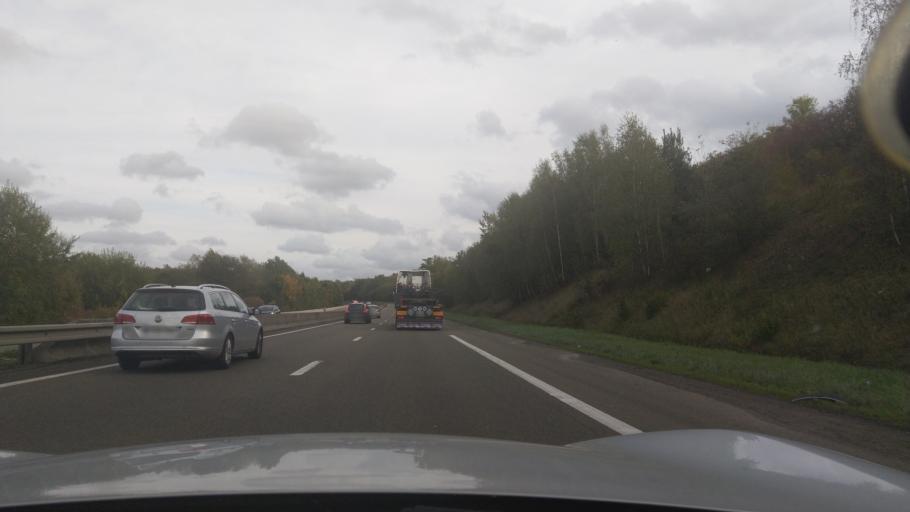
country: FR
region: Ile-de-France
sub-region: Departement du Val-d'Oise
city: Meriel
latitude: 49.0712
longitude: 2.2452
